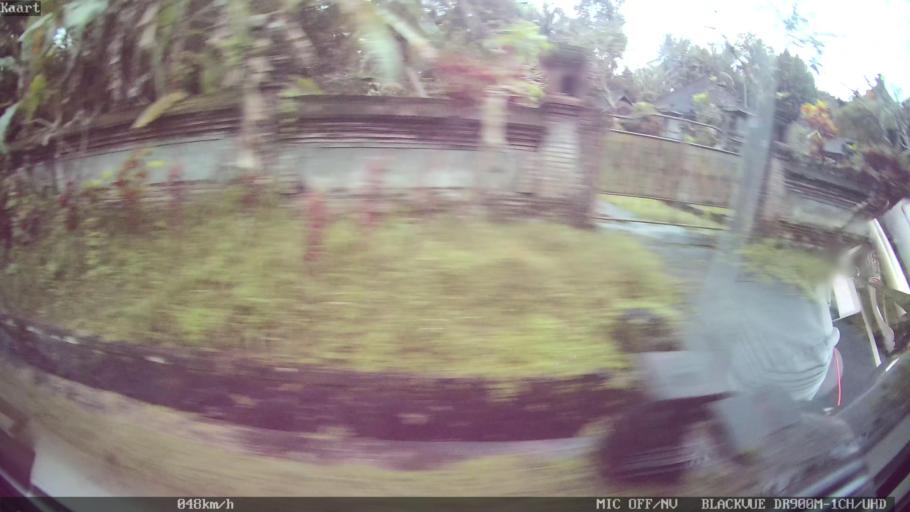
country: ID
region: Bali
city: Banjar Teguan
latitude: -8.4950
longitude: 115.2362
